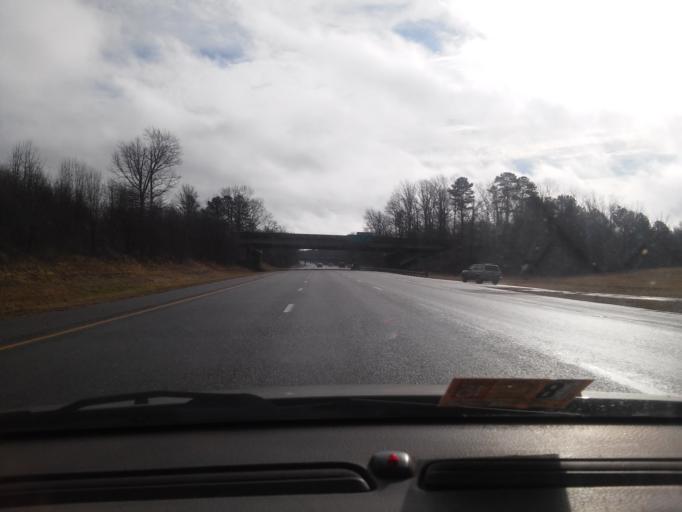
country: US
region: Virginia
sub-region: Henrico County
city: Short Pump
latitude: 37.6355
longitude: -77.5759
